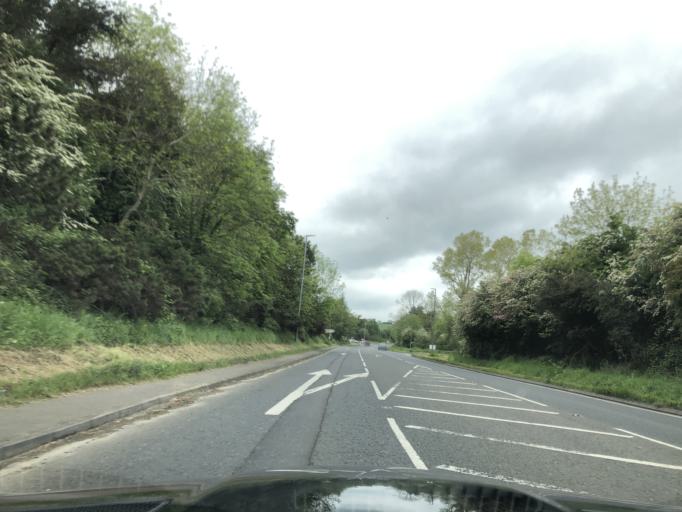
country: GB
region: Northern Ireland
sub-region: Down District
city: Downpatrick
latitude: 54.3517
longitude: -5.7376
